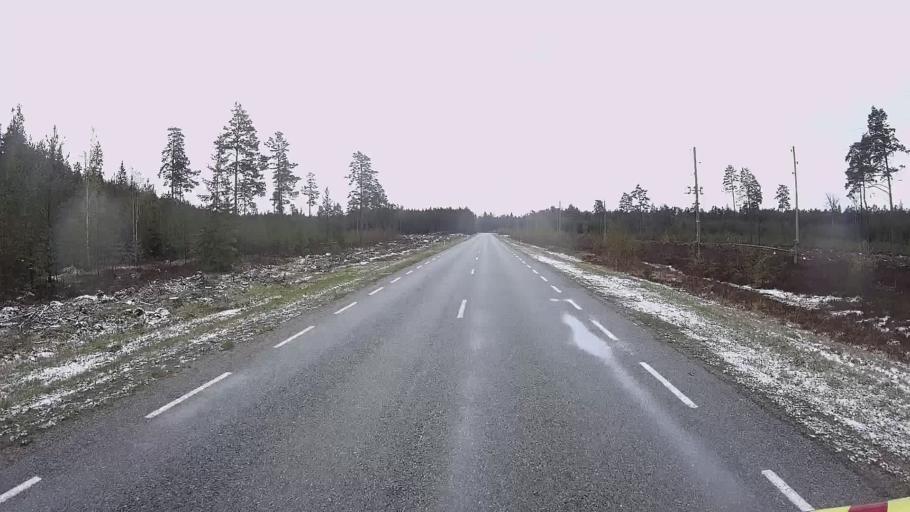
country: EE
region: Hiiumaa
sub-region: Kaerdla linn
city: Kardla
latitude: 59.0162
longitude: 22.6718
